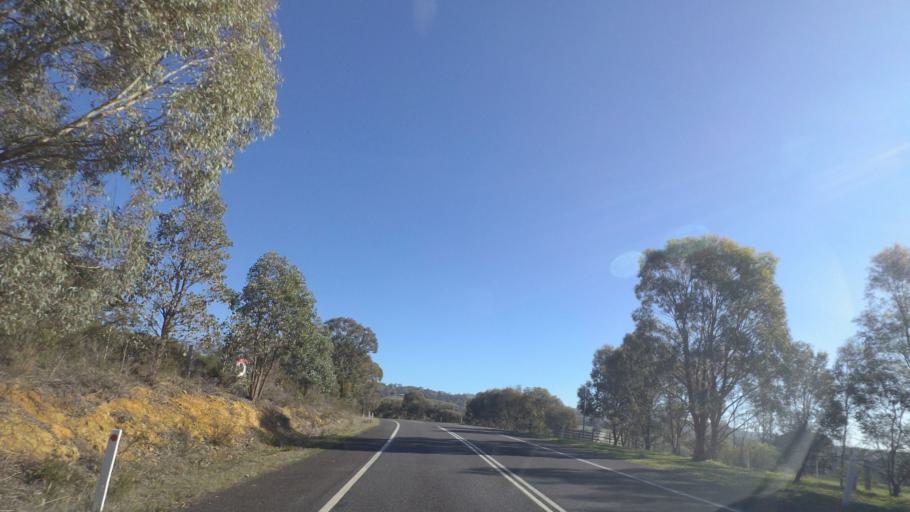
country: AU
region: Victoria
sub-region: Greater Bendigo
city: Kennington
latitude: -36.9106
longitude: 144.3220
